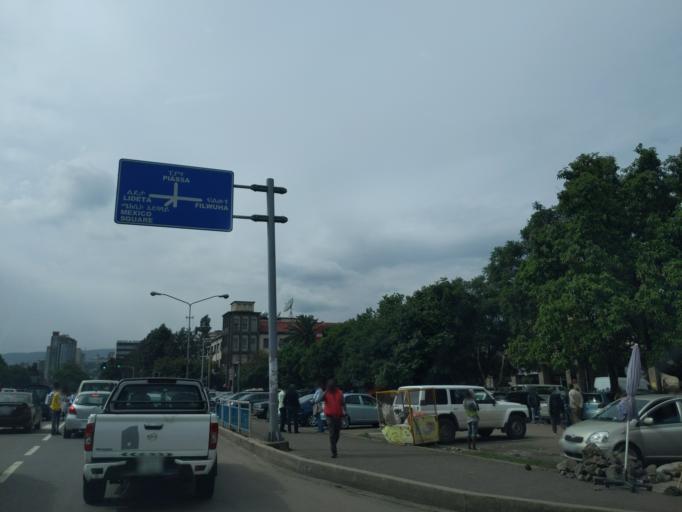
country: ET
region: Adis Abeba
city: Addis Ababa
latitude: 9.0164
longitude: 38.7528
